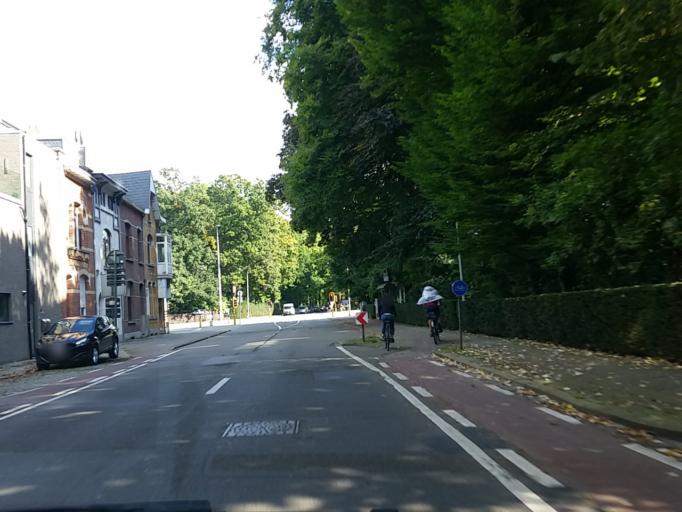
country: BE
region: Flanders
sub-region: Provincie Antwerpen
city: Hove
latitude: 51.1560
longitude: 4.4592
